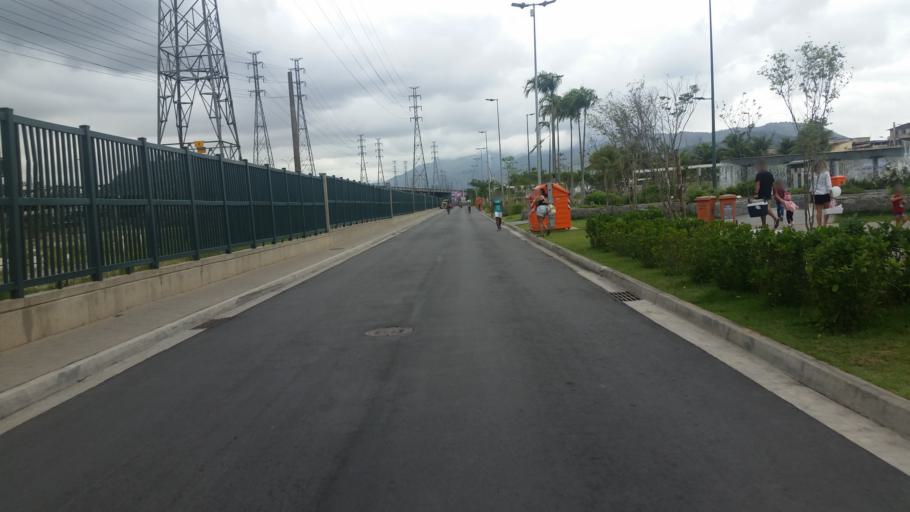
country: BR
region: Rio de Janeiro
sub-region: Sao Joao De Meriti
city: Sao Joao de Meriti
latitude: -22.8579
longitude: -43.3498
